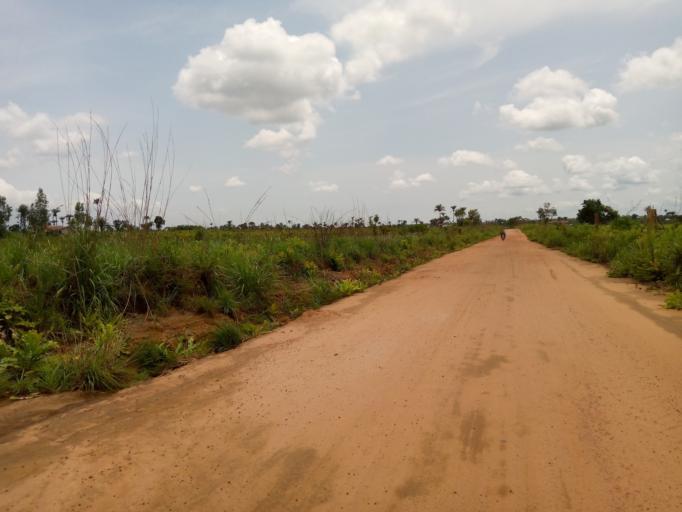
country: SL
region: Western Area
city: Waterloo
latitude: 8.3397
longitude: -12.9448
